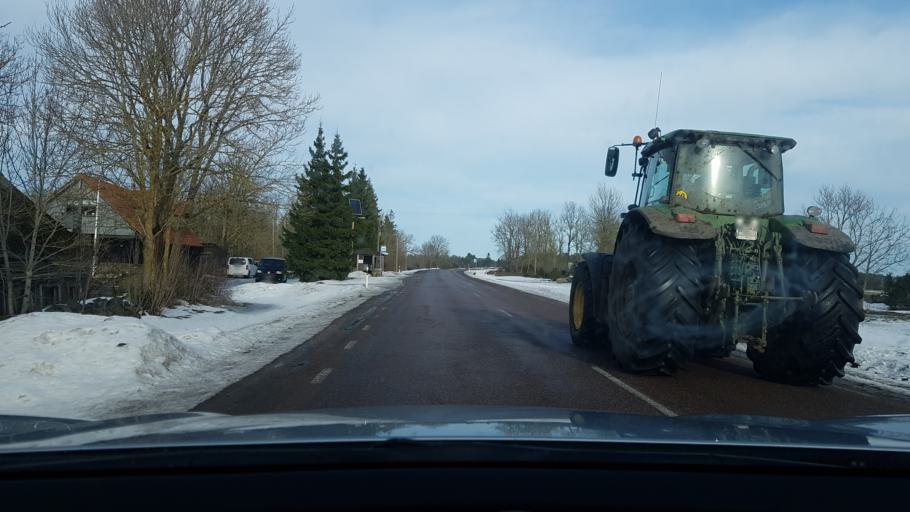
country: EE
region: Saare
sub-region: Kuressaare linn
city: Kuressaare
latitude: 58.3281
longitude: 22.5576
